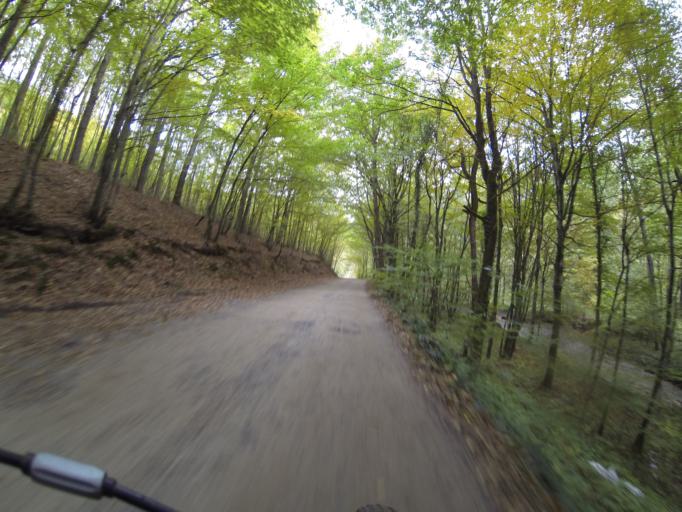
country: RO
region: Gorj
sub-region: Comuna Tismana
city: Sohodol
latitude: 45.0574
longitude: 22.9025
